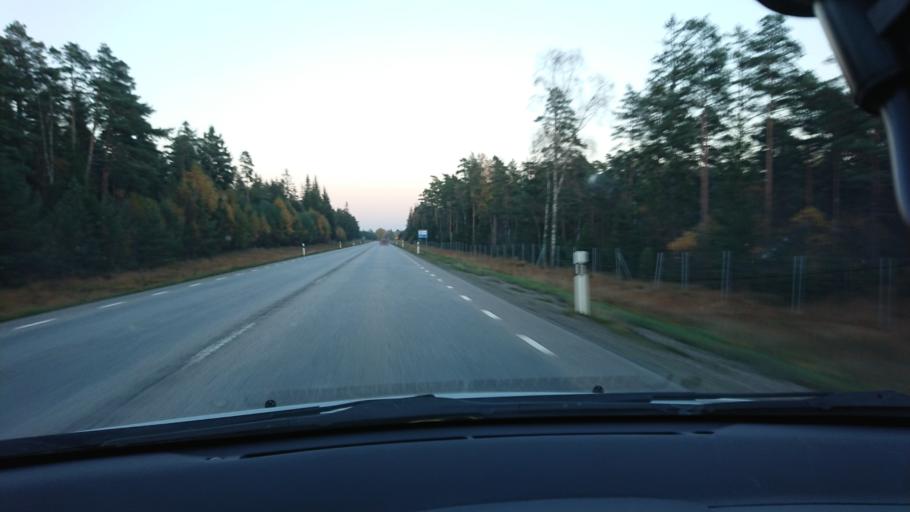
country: SE
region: Halland
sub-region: Laholms Kommun
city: Knared
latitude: 56.7361
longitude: 13.4334
